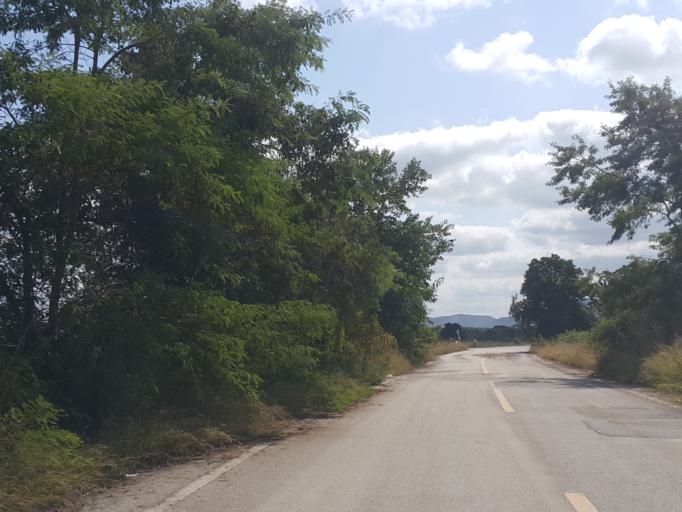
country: TH
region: Lamphun
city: Lamphun
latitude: 18.5501
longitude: 99.0867
